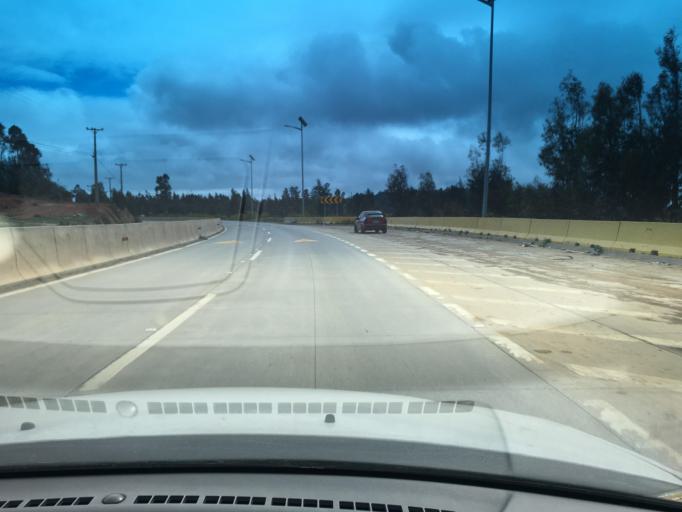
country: CL
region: Valparaiso
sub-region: Provincia de Valparaiso
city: Valparaiso
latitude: -33.0941
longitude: -71.5936
